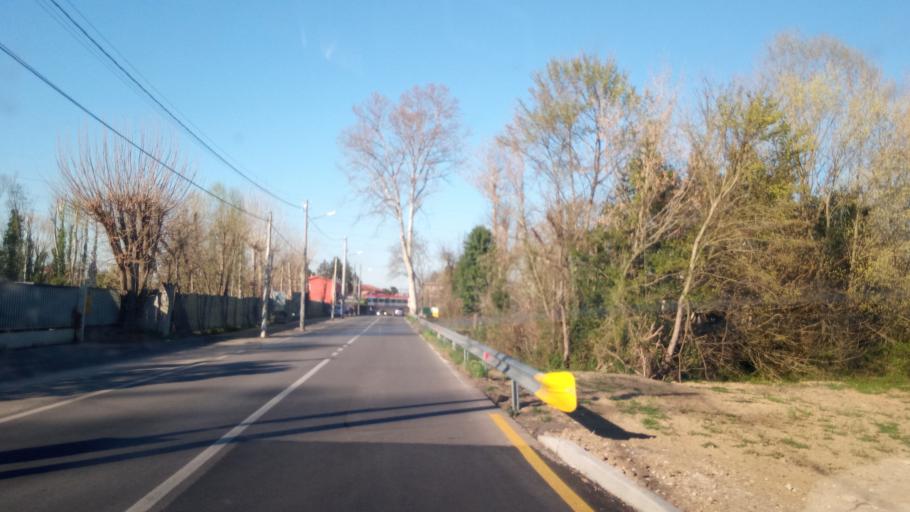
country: IT
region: Veneto
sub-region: Provincia di Padova
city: Padova
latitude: 45.4200
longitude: 11.9091
